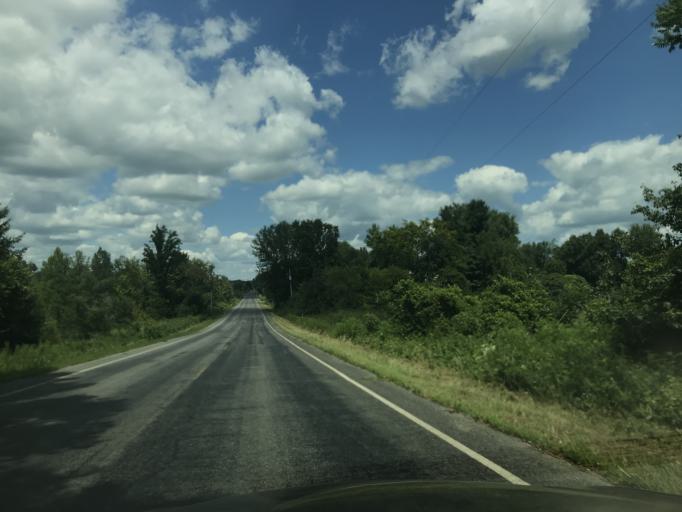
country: US
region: Michigan
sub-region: Eaton County
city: Eaton Rapids
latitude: 42.4610
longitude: -84.5607
